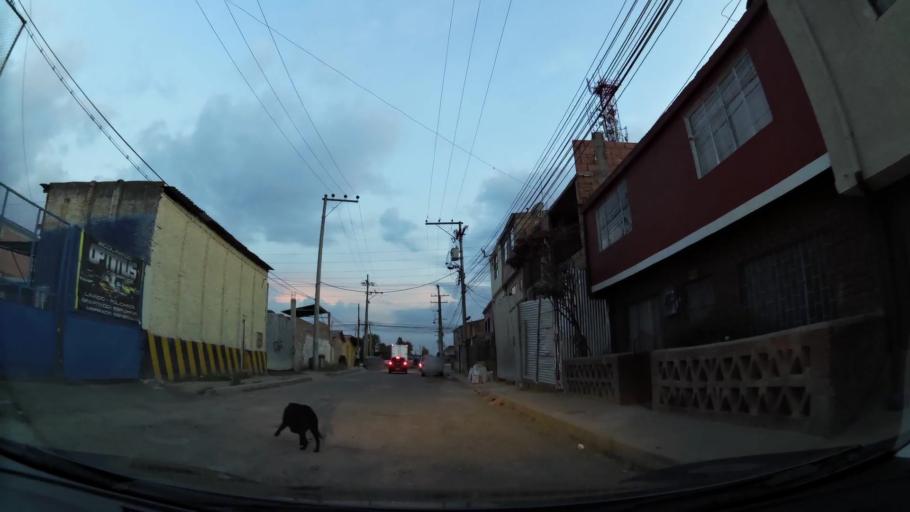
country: CO
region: Cundinamarca
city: Funza
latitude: 4.7188
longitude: -74.2019
